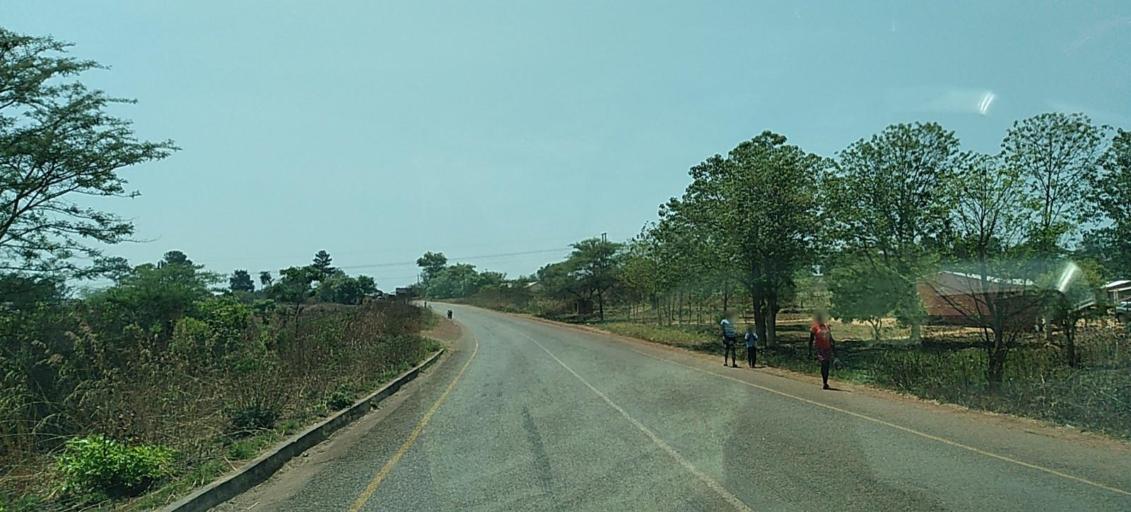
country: ZM
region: North-Western
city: Solwezi
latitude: -12.3955
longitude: 26.2336
